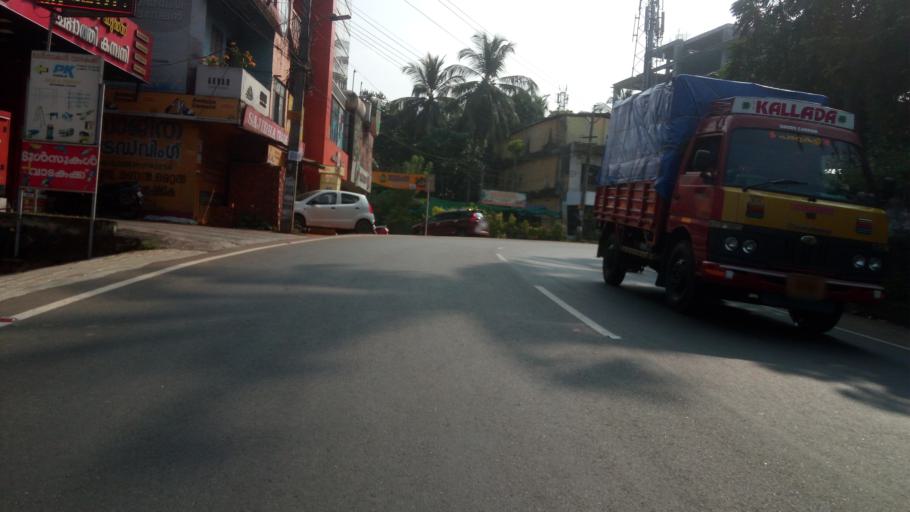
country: IN
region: Kerala
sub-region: Malappuram
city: Malappuram
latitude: 11.0027
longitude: 76.0094
